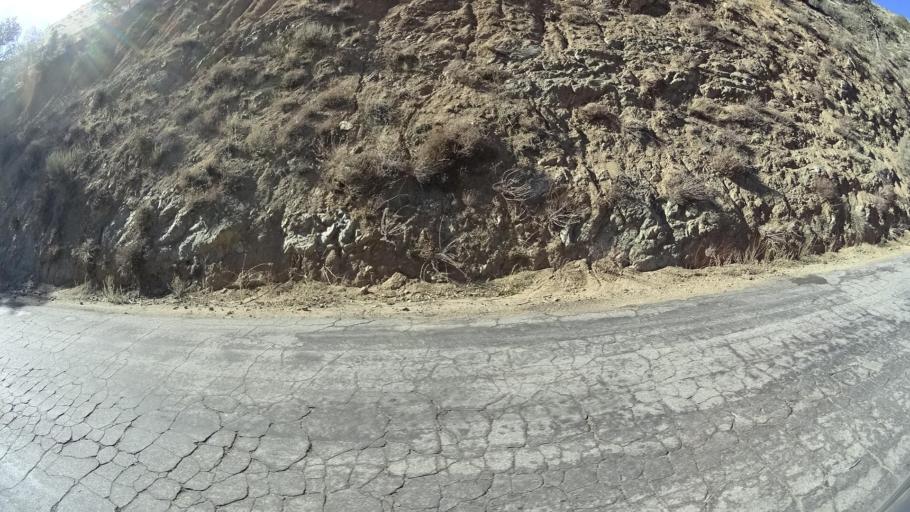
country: US
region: California
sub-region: Kern County
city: Bodfish
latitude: 35.5760
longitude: -118.5046
